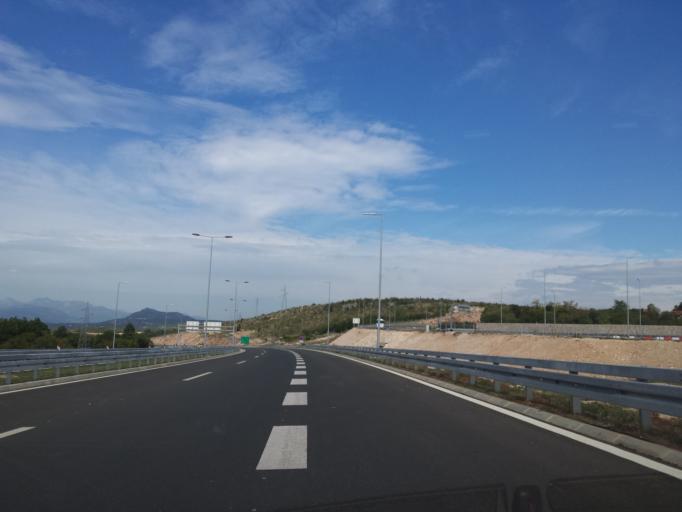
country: BA
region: Federation of Bosnia and Herzegovina
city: Capljina
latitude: 43.1590
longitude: 17.6585
